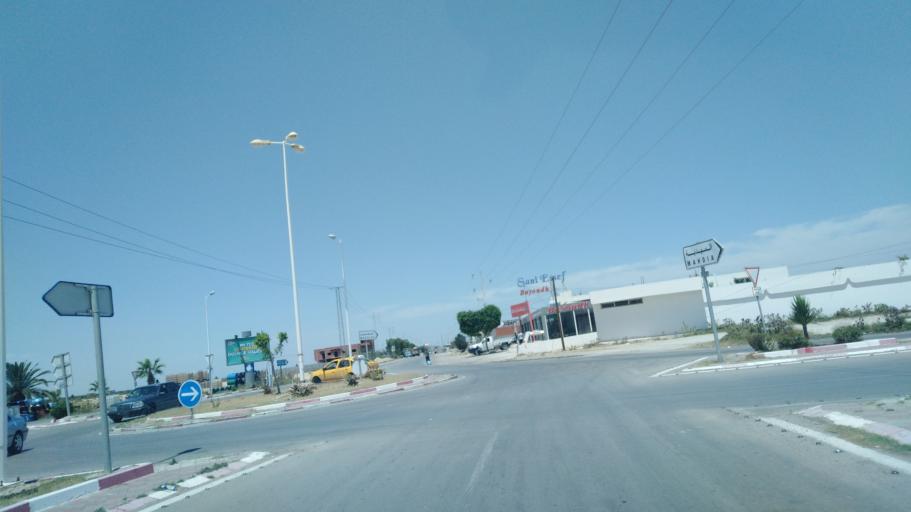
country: TN
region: Al Mahdiyah
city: Ksour Essaf
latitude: 35.4256
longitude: 10.9932
